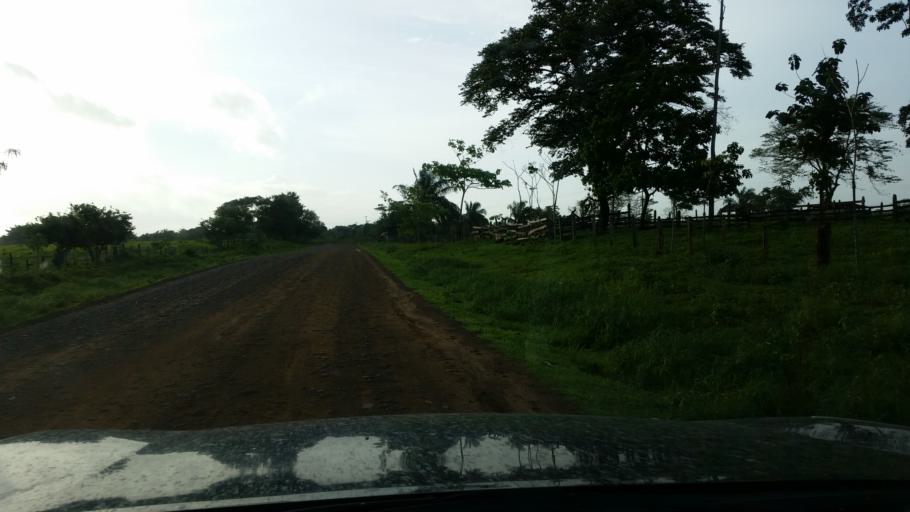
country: NI
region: Atlantico Norte (RAAN)
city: Bonanza
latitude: 14.0653
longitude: -84.0024
